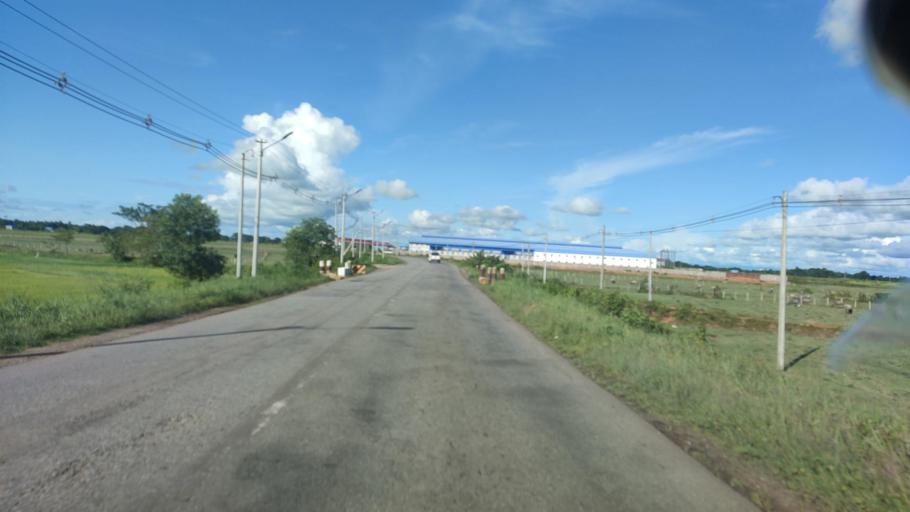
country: MM
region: Bago
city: Bago
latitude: 17.3680
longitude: 96.4657
